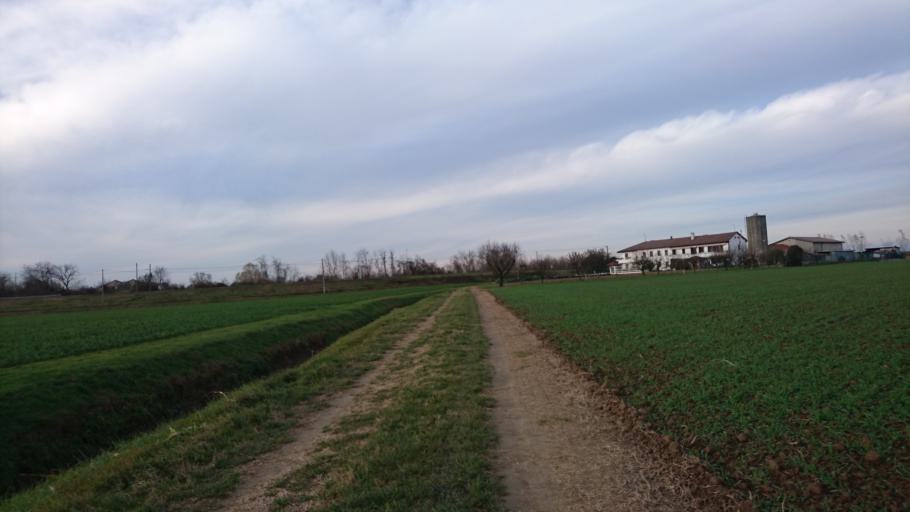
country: IT
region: Veneto
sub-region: Provincia di Padova
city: Polverara
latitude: 45.3271
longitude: 11.9469
